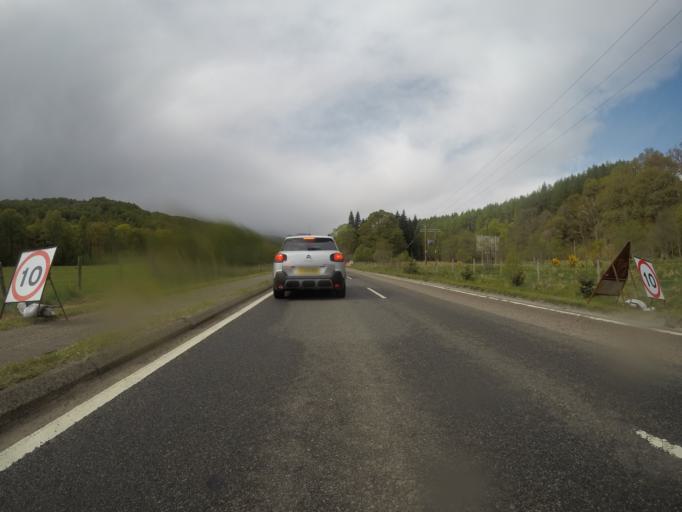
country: GB
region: Scotland
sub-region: Highland
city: Spean Bridge
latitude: 57.0679
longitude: -4.8196
